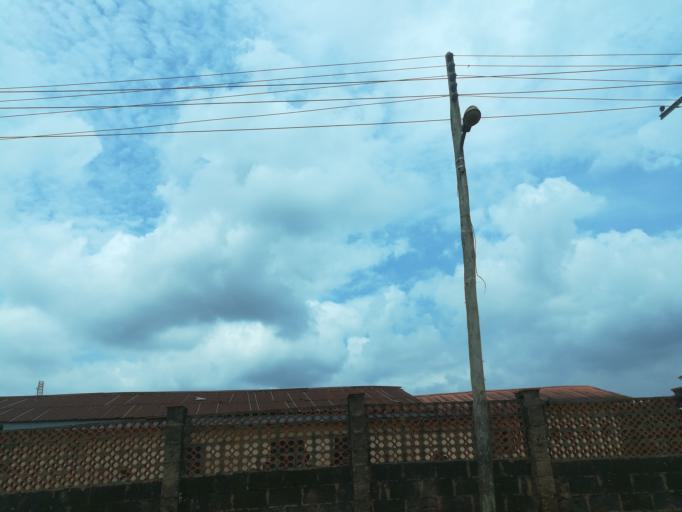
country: NG
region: Lagos
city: Ejirin
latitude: 6.6458
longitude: 3.7132
